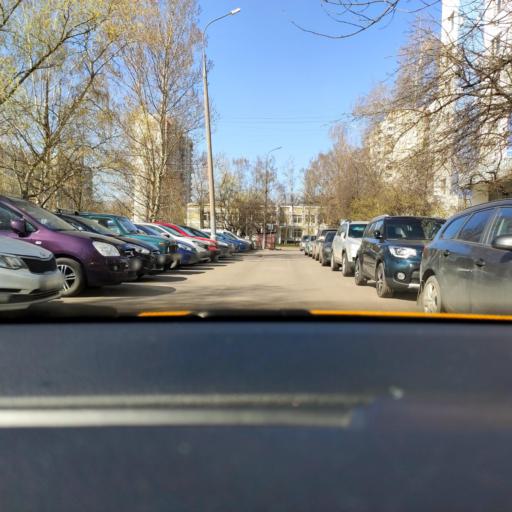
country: RU
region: Moskovskaya
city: Vostochnoe Degunino
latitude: 55.8903
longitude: 37.5626
